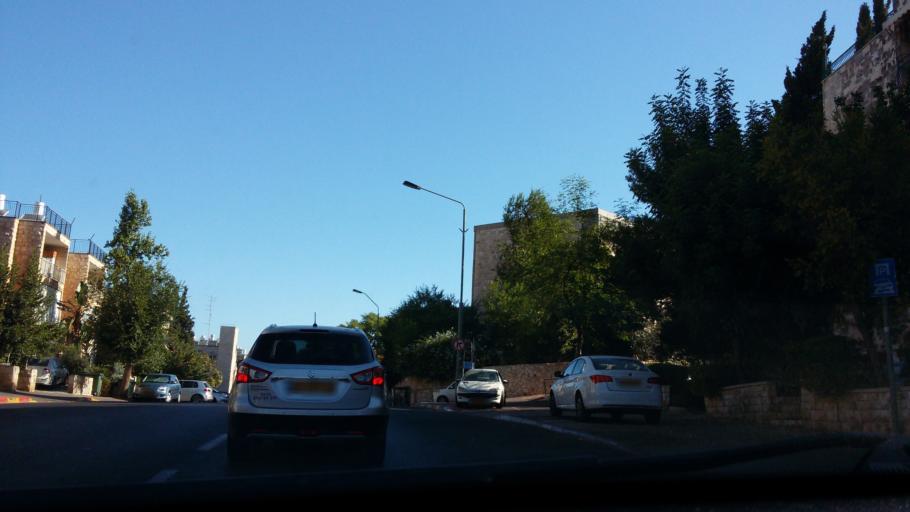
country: IL
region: Jerusalem
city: Jerusalem
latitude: 31.7656
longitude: 35.2061
